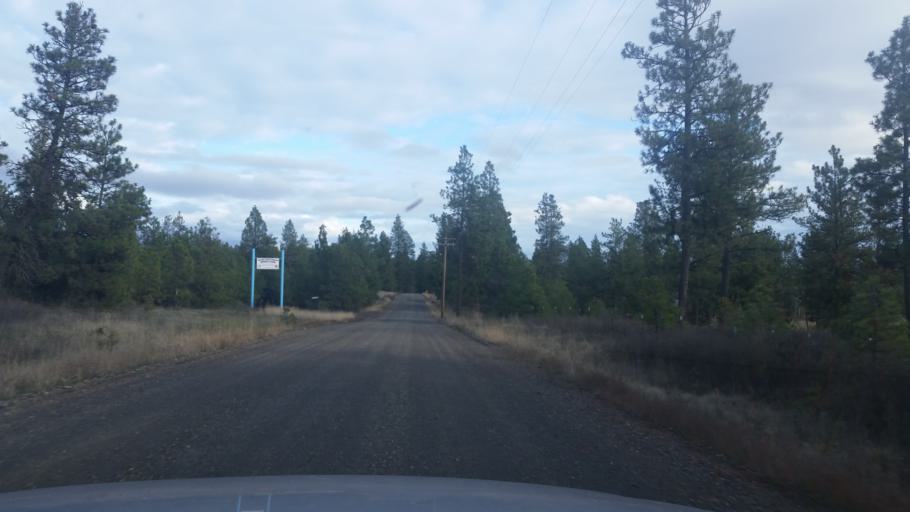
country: US
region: Washington
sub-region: Spokane County
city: Cheney
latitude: 47.4346
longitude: -117.4505
